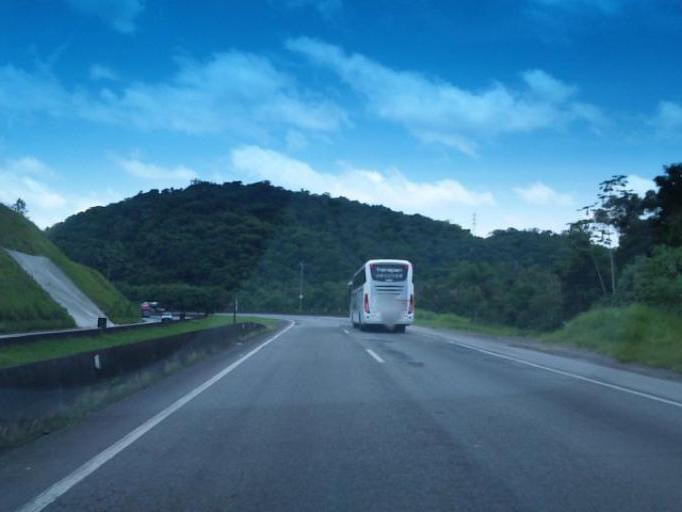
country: BR
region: Sao Paulo
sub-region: Juquia
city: Juquia
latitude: -24.3799
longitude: -47.7135
